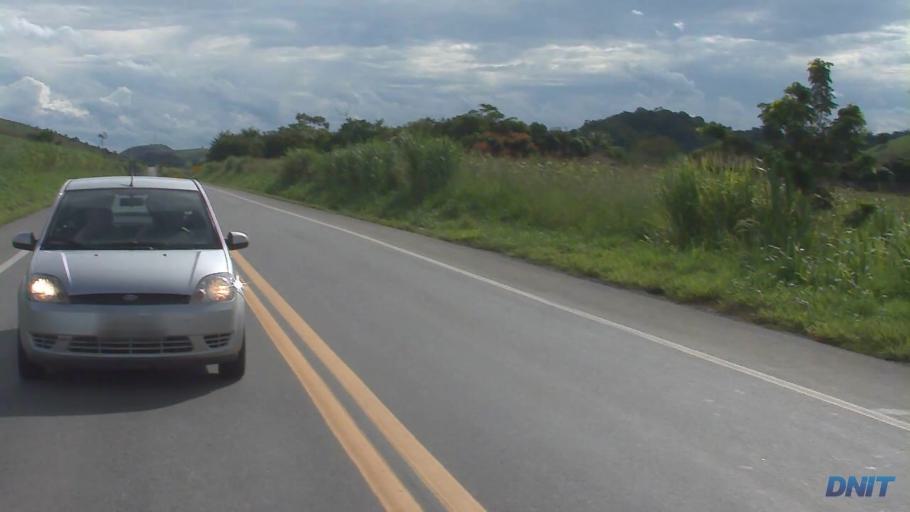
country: BR
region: Minas Gerais
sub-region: Belo Oriente
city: Belo Oriente
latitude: -19.1942
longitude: -42.2789
